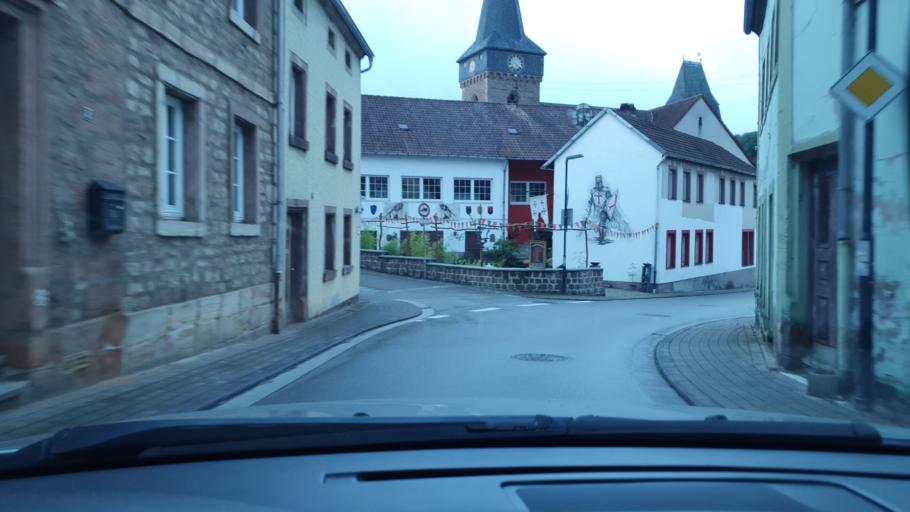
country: DE
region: Rheinland-Pfalz
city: Wallhalben
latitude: 49.3166
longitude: 7.5246
